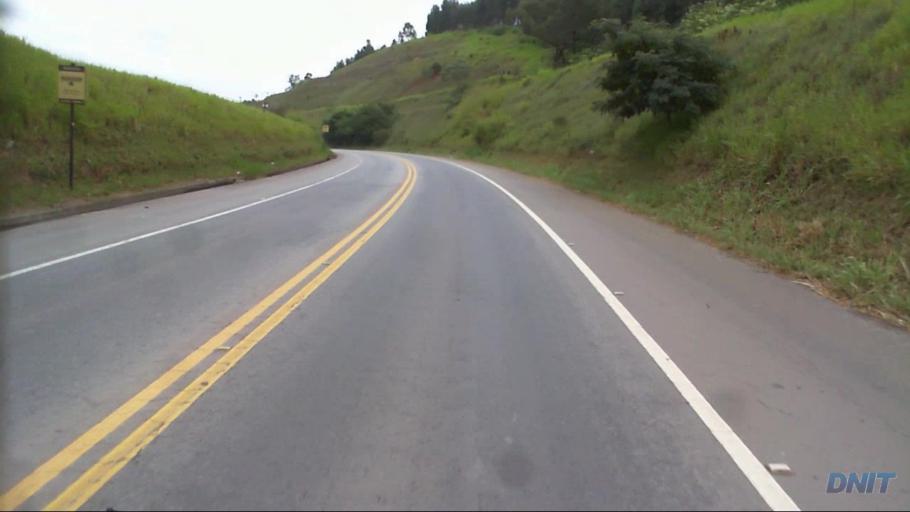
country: BR
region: Minas Gerais
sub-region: Coronel Fabriciano
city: Coronel Fabriciano
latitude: -19.5210
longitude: -42.5814
